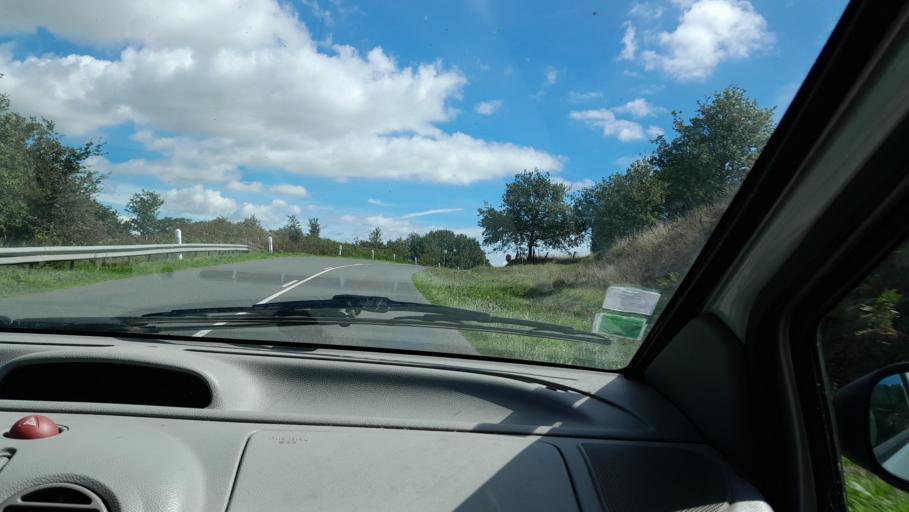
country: FR
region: Pays de la Loire
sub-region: Departement de la Mayenne
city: Cosse-le-Vivien
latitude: 47.9544
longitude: -0.9369
